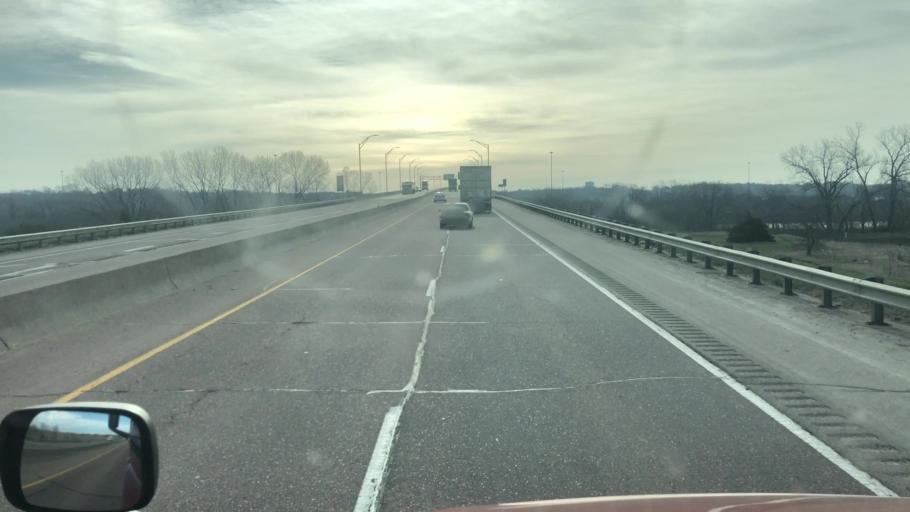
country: US
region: Nebraska
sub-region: Dakota County
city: South Sioux City
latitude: 42.4475
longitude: -96.3863
